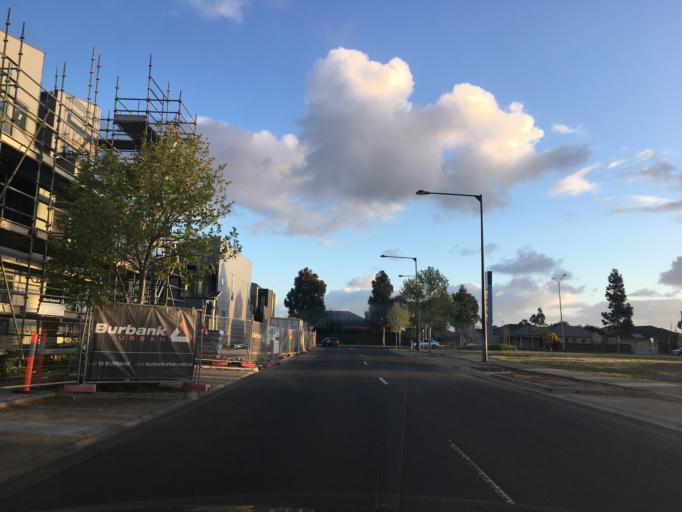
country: AU
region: Victoria
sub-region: Wyndham
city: Williams Landing
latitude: -37.8839
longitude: 144.7381
